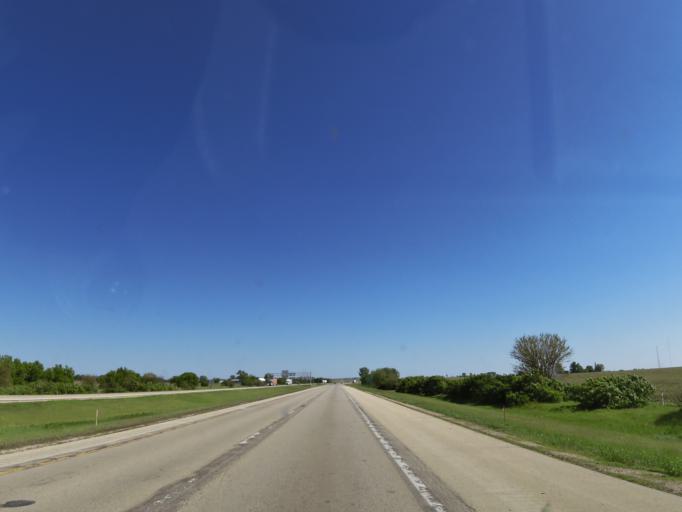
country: US
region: Illinois
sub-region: Ogle County
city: Rochelle
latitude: 41.8929
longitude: -89.0144
